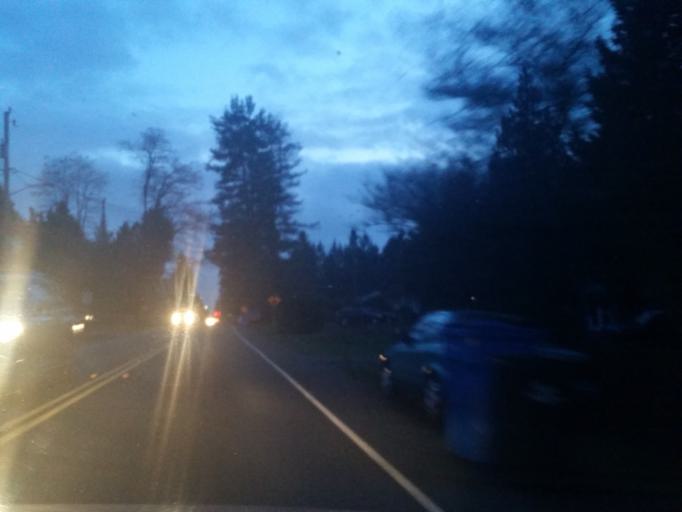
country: US
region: Washington
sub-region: King County
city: Shoreline
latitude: 47.7607
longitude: -122.3189
